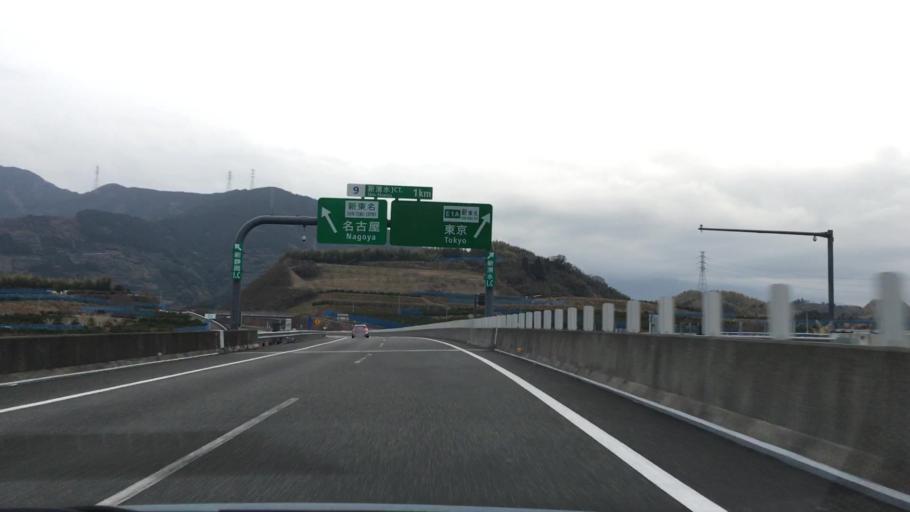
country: JP
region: Shizuoka
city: Shizuoka-shi
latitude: 35.0693
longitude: 138.4773
